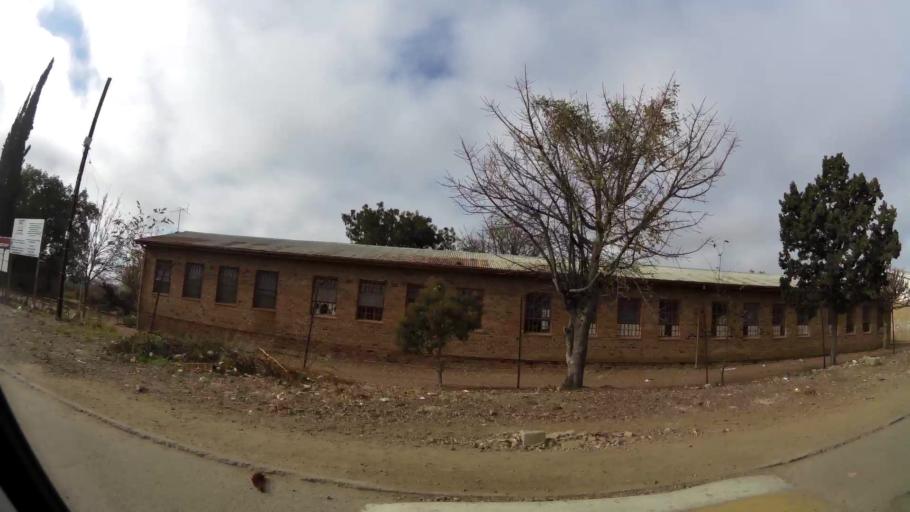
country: ZA
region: Limpopo
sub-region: Capricorn District Municipality
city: Polokwane
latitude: -23.8490
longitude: 29.3866
